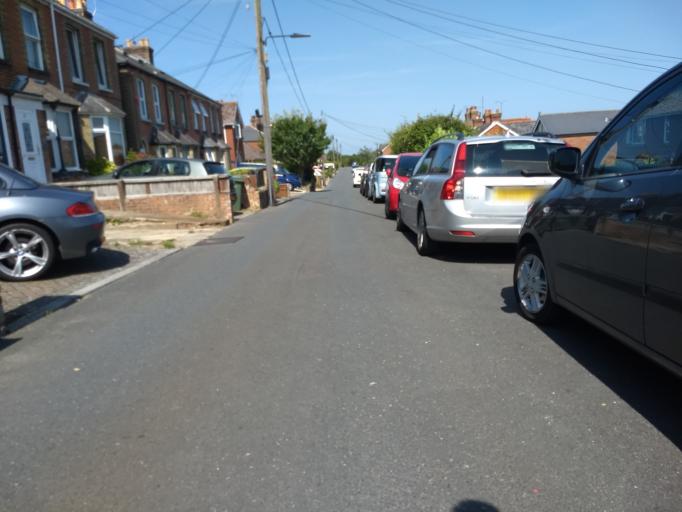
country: GB
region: England
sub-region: Isle of Wight
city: Newport
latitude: 50.6920
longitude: -1.3199
